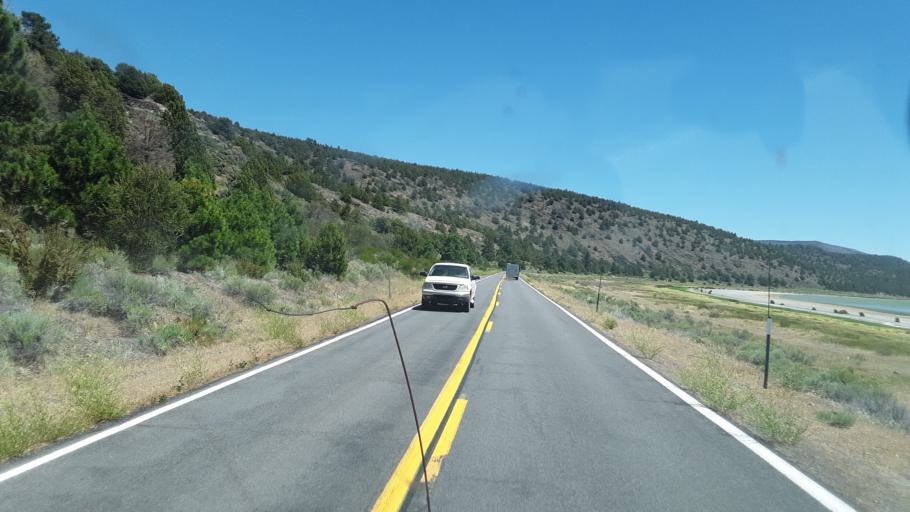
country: US
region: California
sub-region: Lassen County
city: Susanville
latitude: 40.7217
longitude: -120.6866
